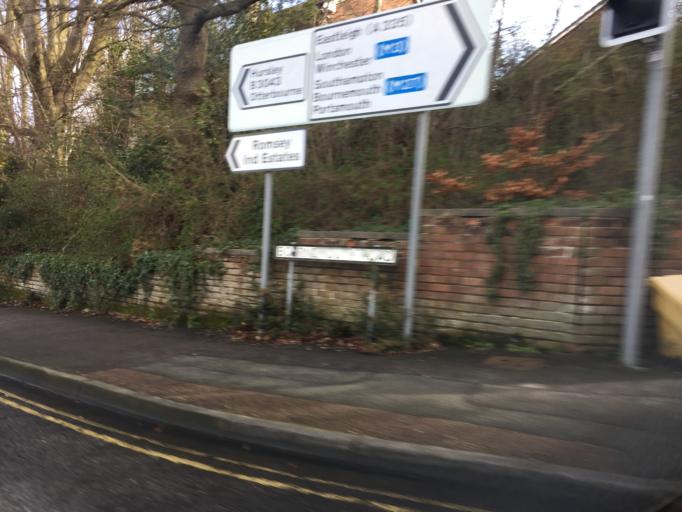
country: GB
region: England
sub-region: Hampshire
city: Chandlers Ford
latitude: 50.9812
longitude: -1.3842
